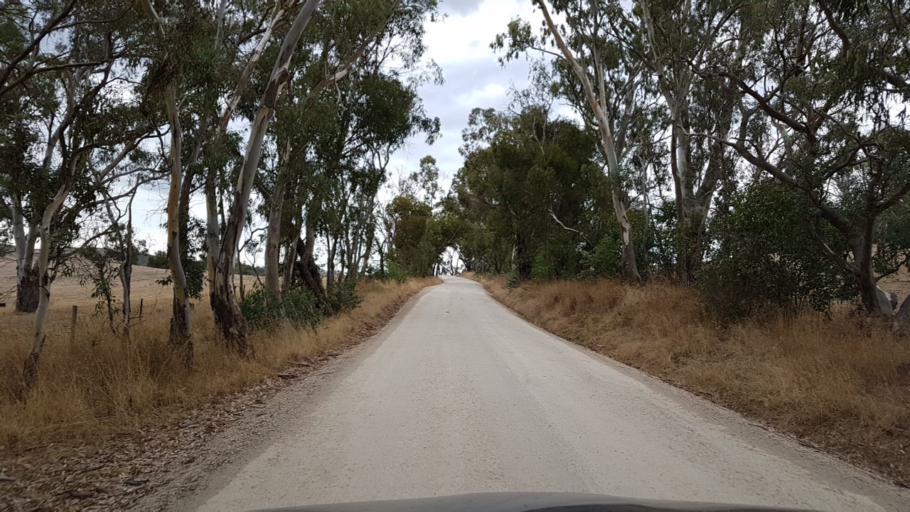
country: AU
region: South Australia
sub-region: Adelaide Hills
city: Gumeracha
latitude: -34.7967
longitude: 138.8339
